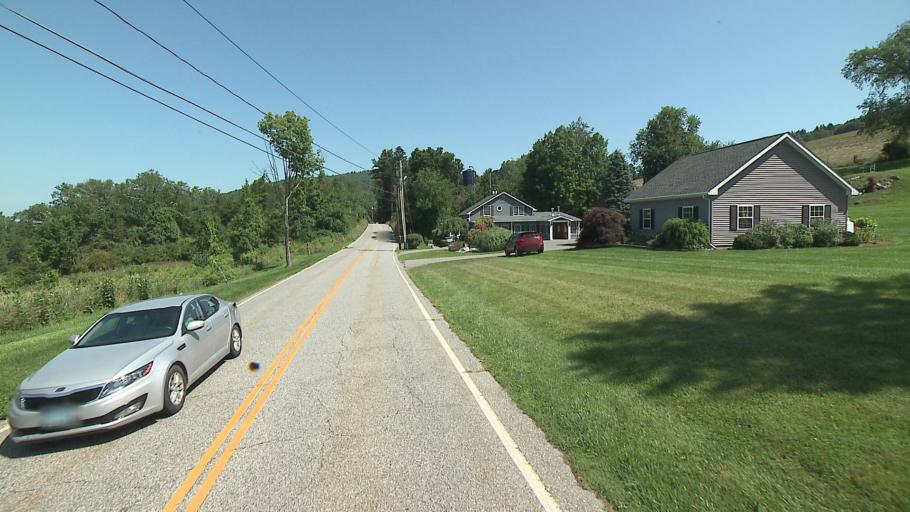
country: US
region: New York
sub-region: Dutchess County
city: Pine Plains
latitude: 41.9087
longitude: -73.4922
